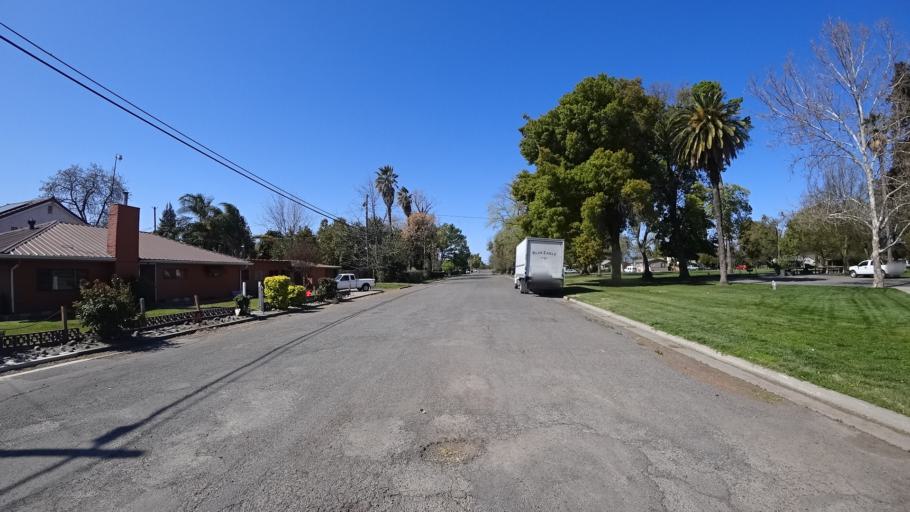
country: US
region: California
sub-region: Glenn County
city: Hamilton City
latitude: 39.7397
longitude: -122.0127
